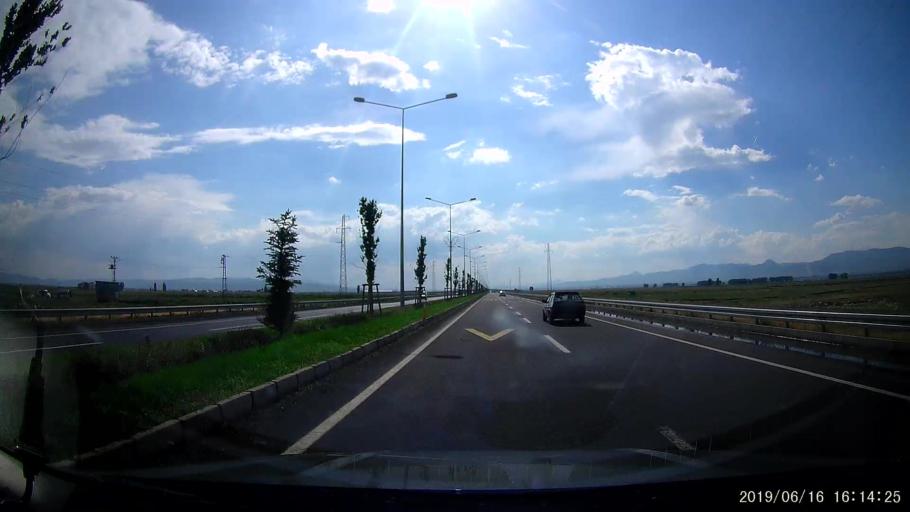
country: TR
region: Erzurum
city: Erzurum
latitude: 39.9607
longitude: 41.2496
